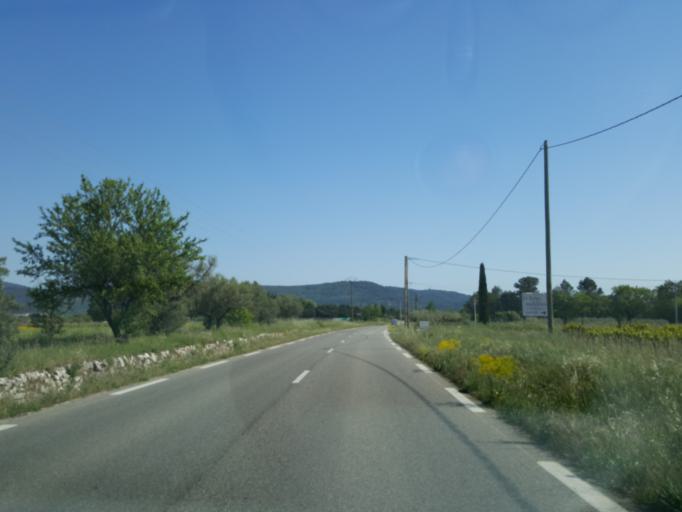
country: FR
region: Provence-Alpes-Cote d'Azur
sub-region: Departement du Var
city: La Roquebrussanne
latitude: 43.3312
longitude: 5.9814
